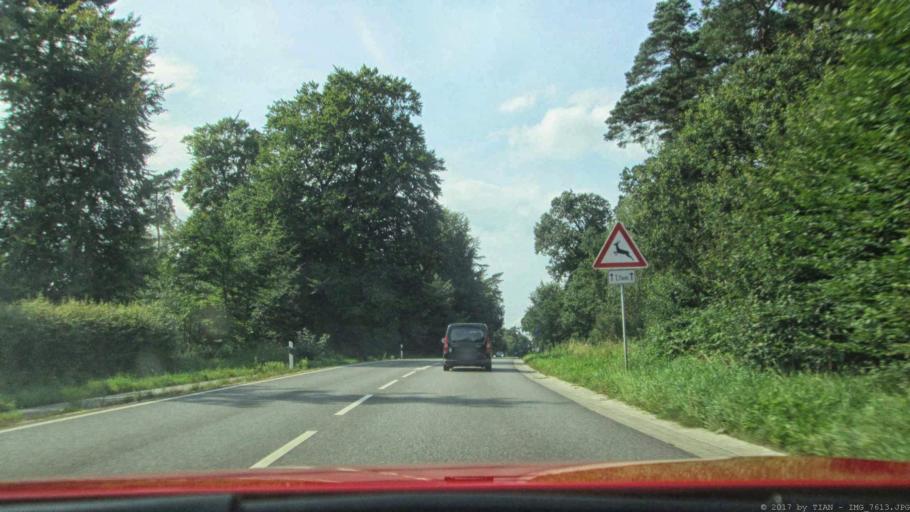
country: DE
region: Schleswig-Holstein
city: Hamwarde
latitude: 53.4247
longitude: 10.4135
